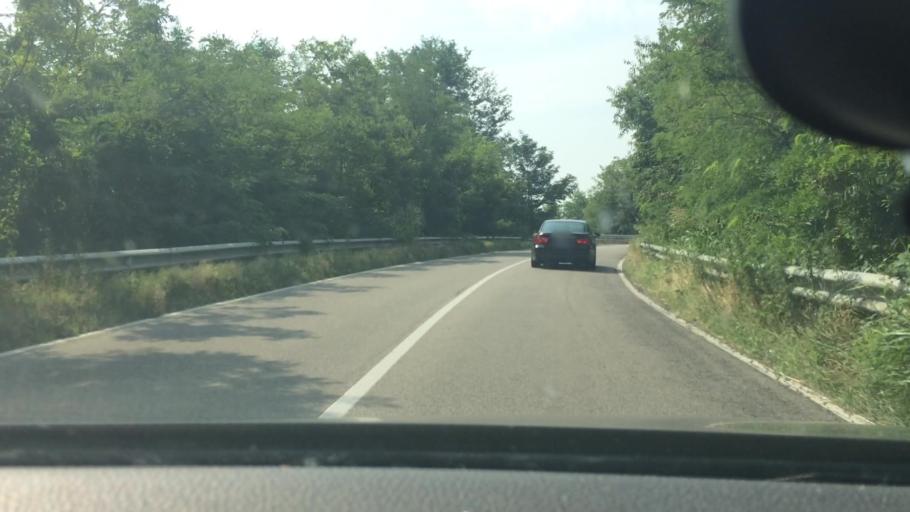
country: IT
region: Lombardy
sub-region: Citta metropolitana di Milano
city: Busto Garolfo
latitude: 45.5418
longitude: 8.8978
